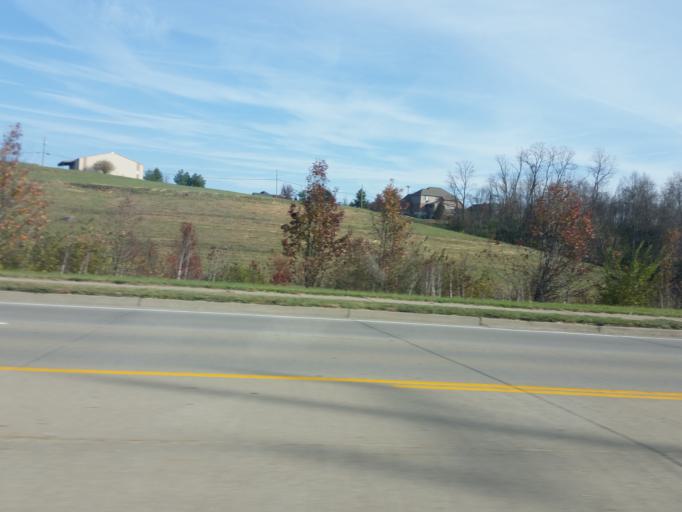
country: US
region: Kentucky
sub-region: Campbell County
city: Alexandria
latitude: 38.9483
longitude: -84.3937
